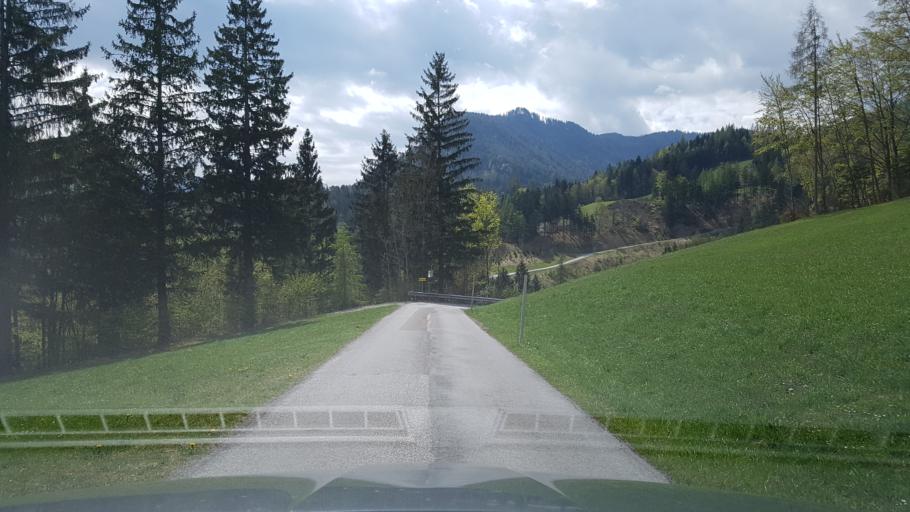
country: AT
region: Salzburg
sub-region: Politischer Bezirk Sankt Johann im Pongau
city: Werfen
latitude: 47.4622
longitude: 13.1886
